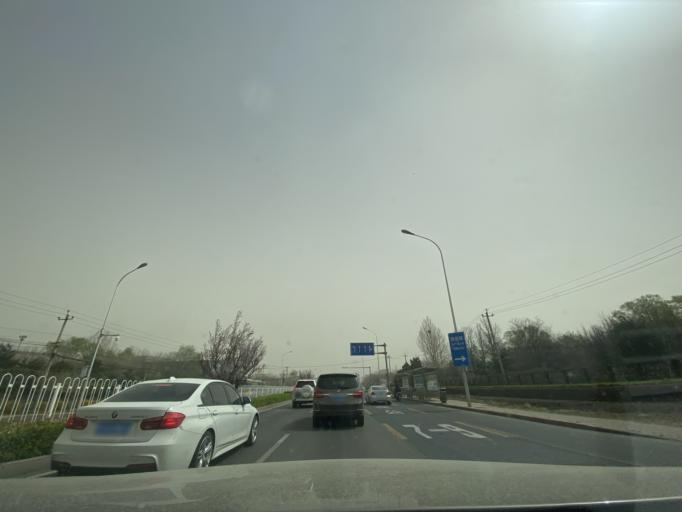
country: CN
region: Beijing
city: Sijiqing
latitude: 39.9457
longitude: 116.2609
